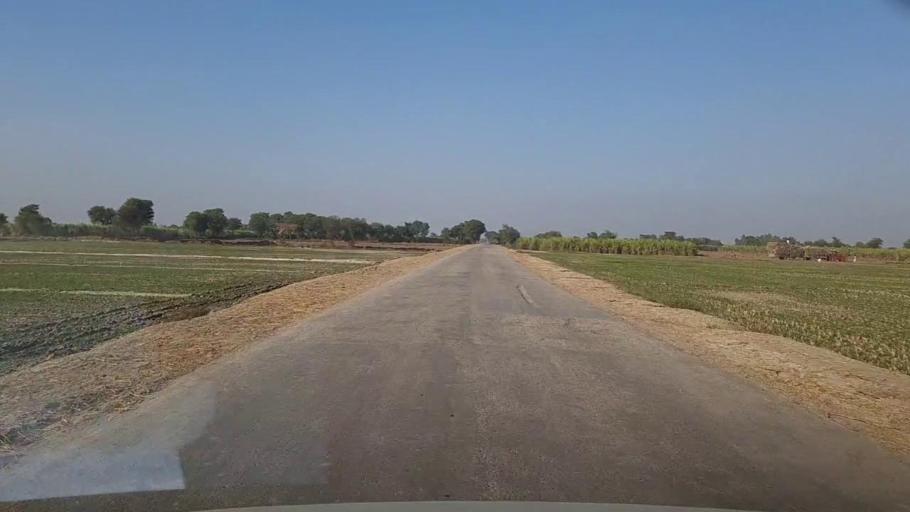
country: PK
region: Sindh
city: Dadu
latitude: 26.8470
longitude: 67.7937
